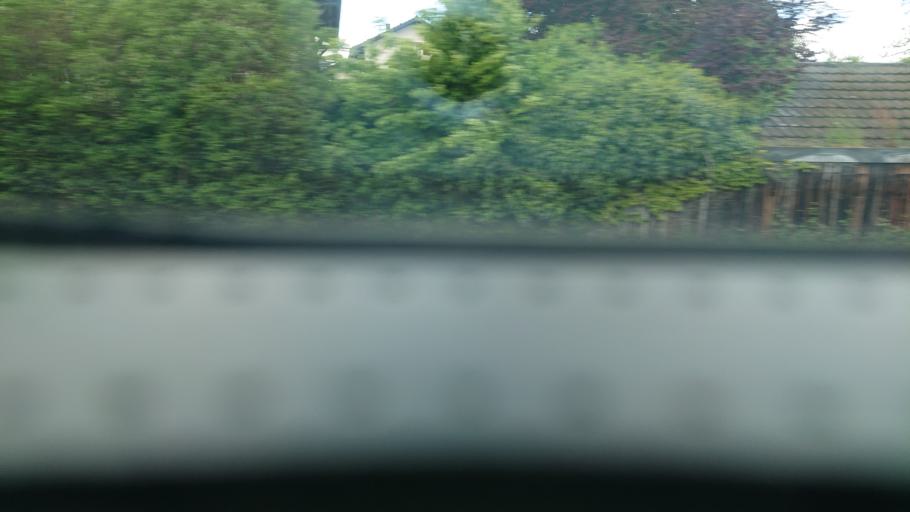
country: CH
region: Vaud
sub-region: Nyon District
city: Coppet
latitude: 46.3208
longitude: 6.1891
